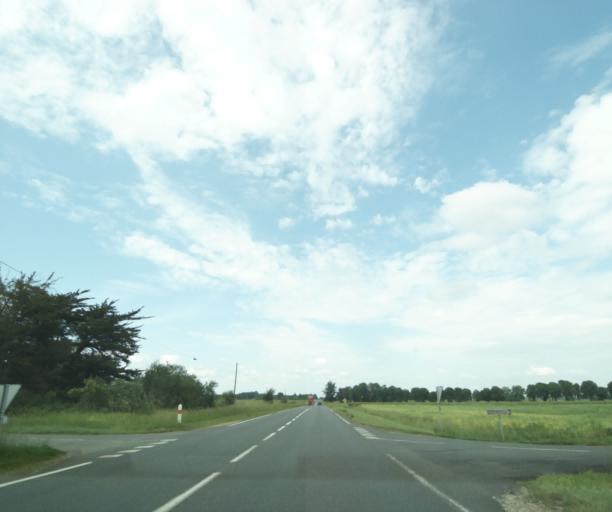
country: FR
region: Pays de la Loire
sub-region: Departement de Maine-et-Loire
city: Montreuil-Bellay
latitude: 47.1473
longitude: -0.1512
